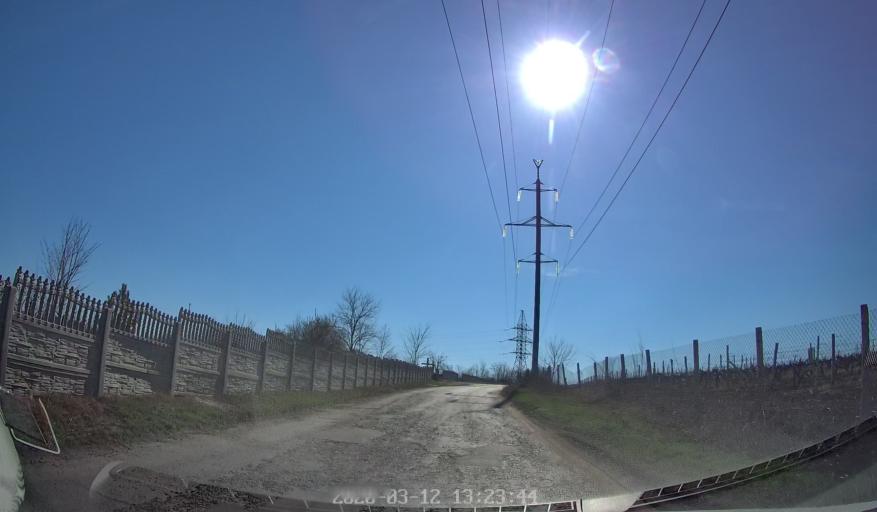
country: MD
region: Laloveni
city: Ialoveni
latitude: 46.9432
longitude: 28.8324
